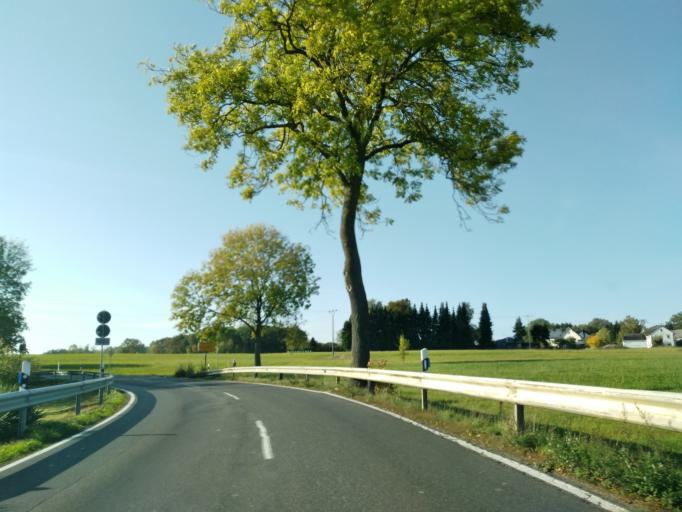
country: DE
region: Rheinland-Pfalz
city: Asbach
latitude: 50.6686
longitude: 7.3817
